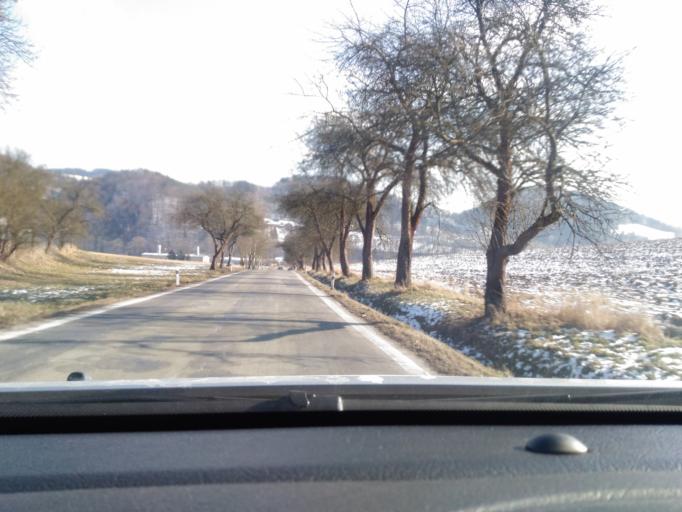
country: CZ
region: South Moravian
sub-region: Okres Brno-Venkov
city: Nedvedice
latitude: 49.4732
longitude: 16.3385
